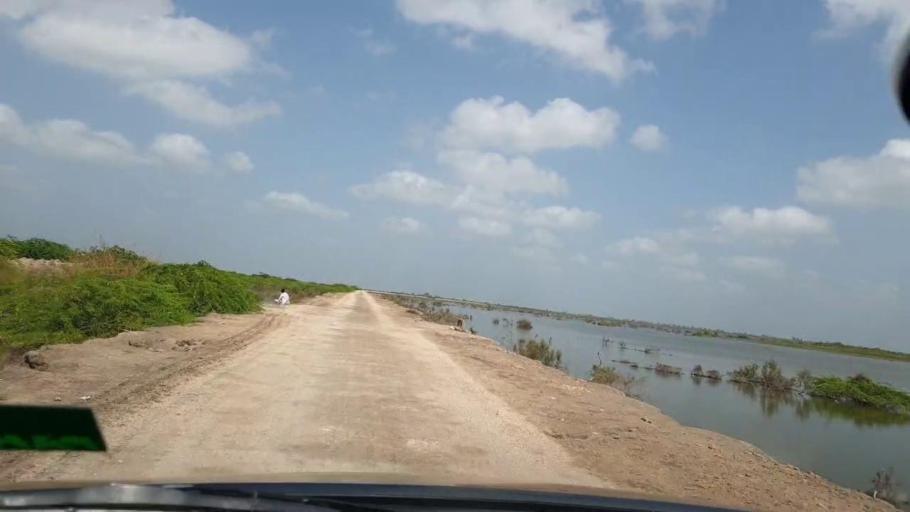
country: PK
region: Sindh
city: Kadhan
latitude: 24.5778
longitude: 69.1427
